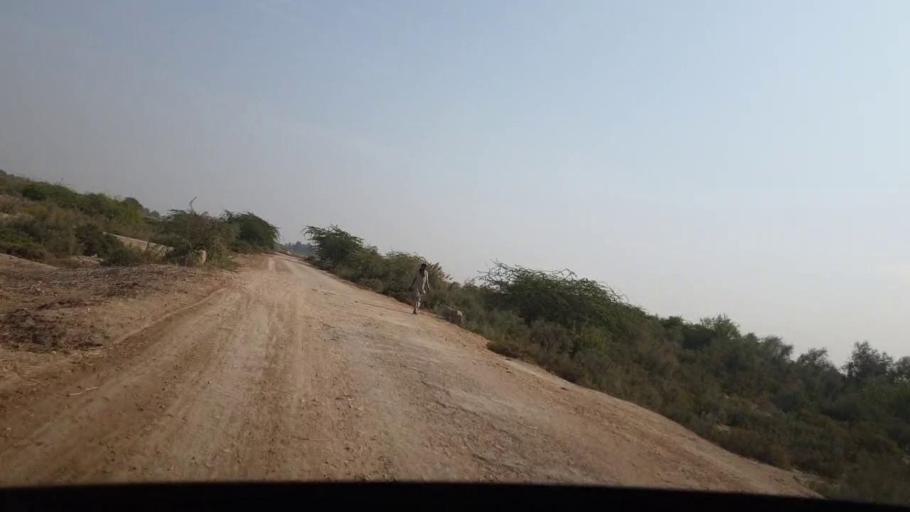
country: PK
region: Sindh
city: Chuhar Jamali
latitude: 24.2692
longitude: 67.9343
